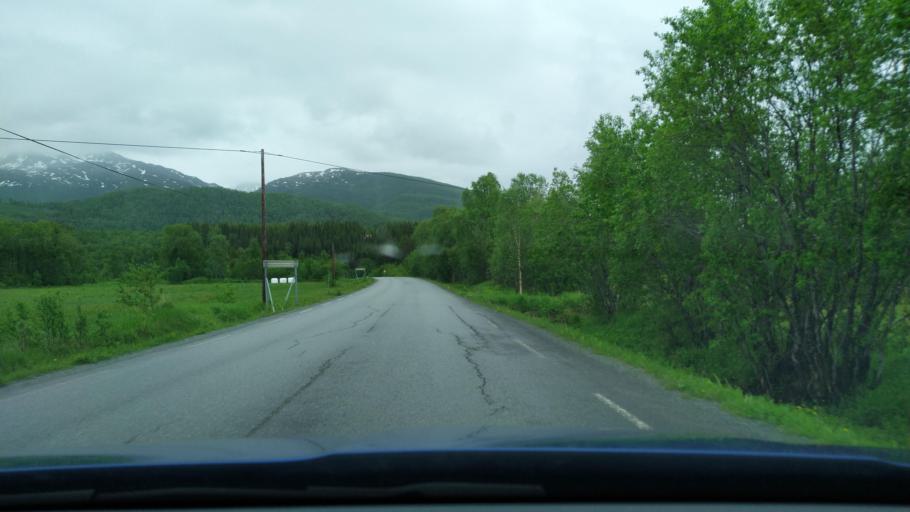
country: NO
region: Troms
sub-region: Dyroy
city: Brostadbotn
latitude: 69.0768
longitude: 17.6985
